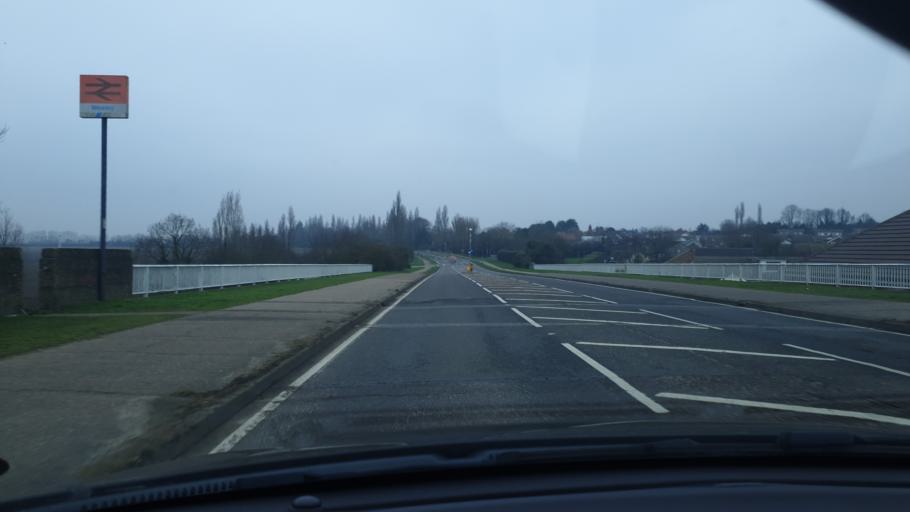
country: GB
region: England
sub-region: Essex
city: Little Clacton
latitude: 51.8531
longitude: 1.1161
